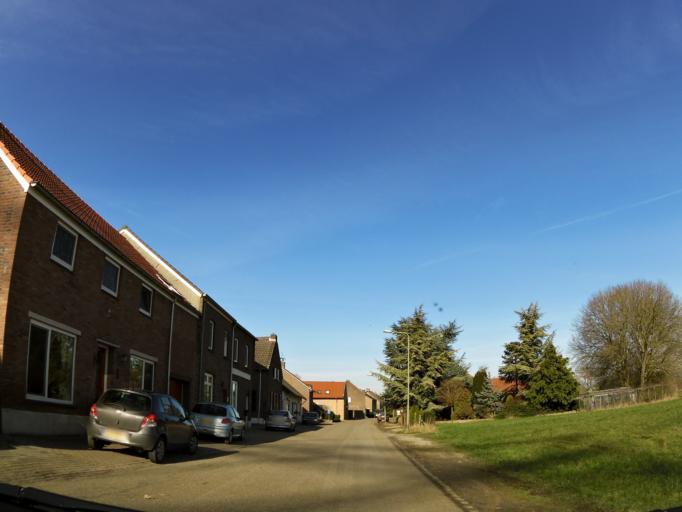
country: NL
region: Limburg
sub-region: Gemeente Sittard-Geleen
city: Born
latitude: 51.0595
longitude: 5.8054
